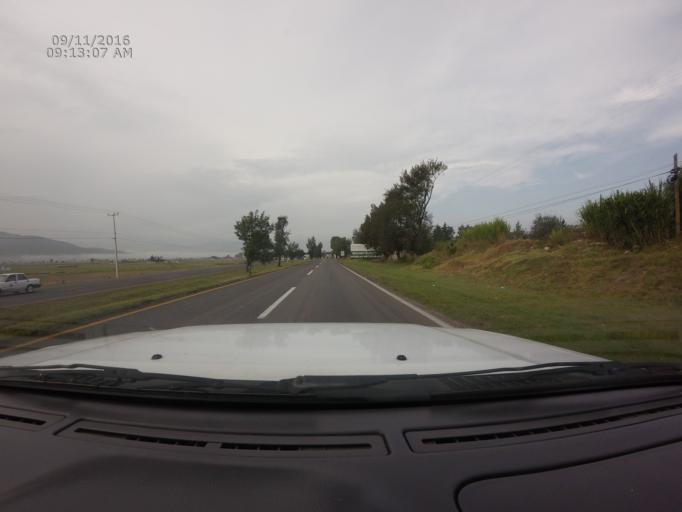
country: MX
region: Michoacan
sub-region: Morelia
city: La Mintzita (Piedra Dura)
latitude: 19.5855
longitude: -101.3050
